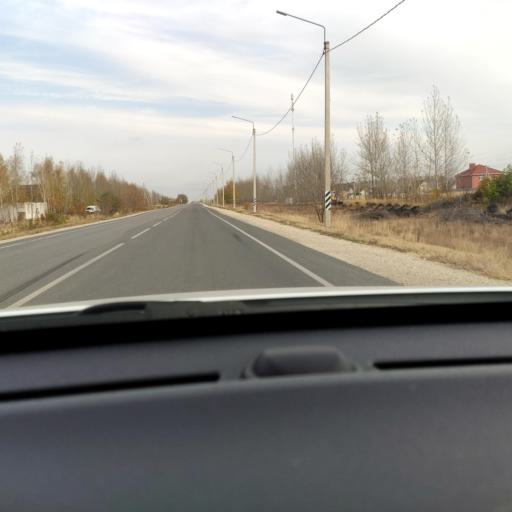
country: RU
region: Voronezj
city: Novaya Usman'
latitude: 51.6664
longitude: 39.4519
